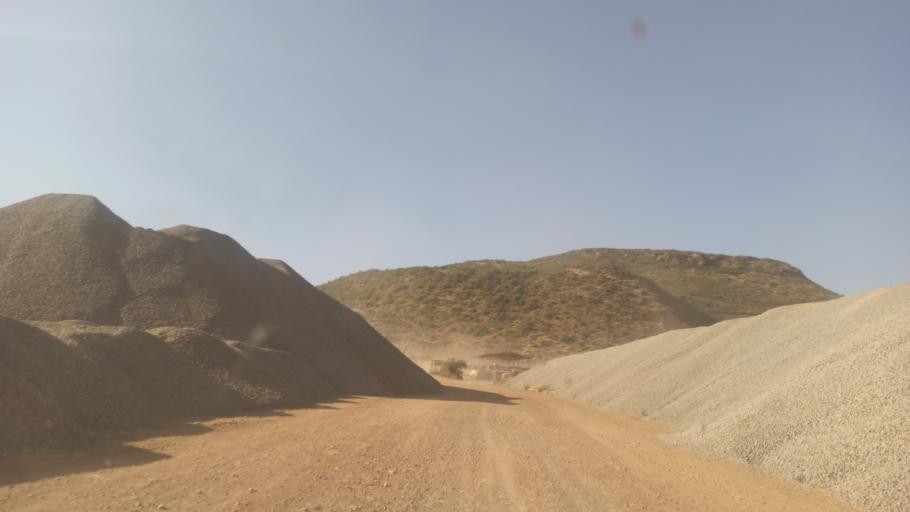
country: ET
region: Oromiya
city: Ziway
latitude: 7.9334
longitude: 38.6155
